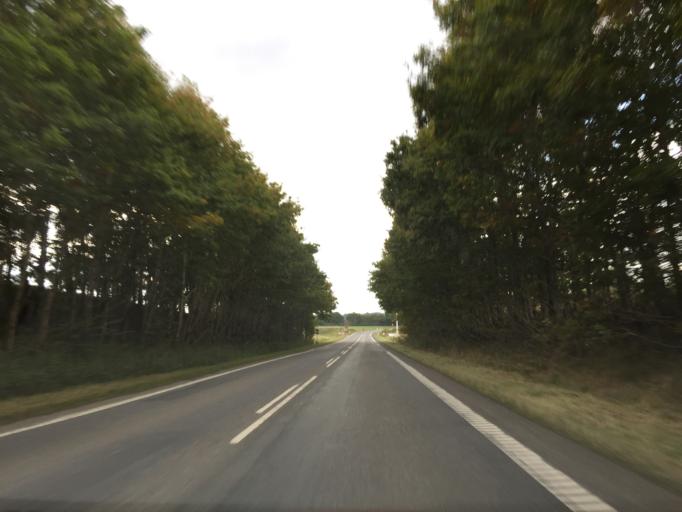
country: DK
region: Central Jutland
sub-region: Favrskov Kommune
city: Ulstrup
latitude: 56.3156
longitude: 9.7780
